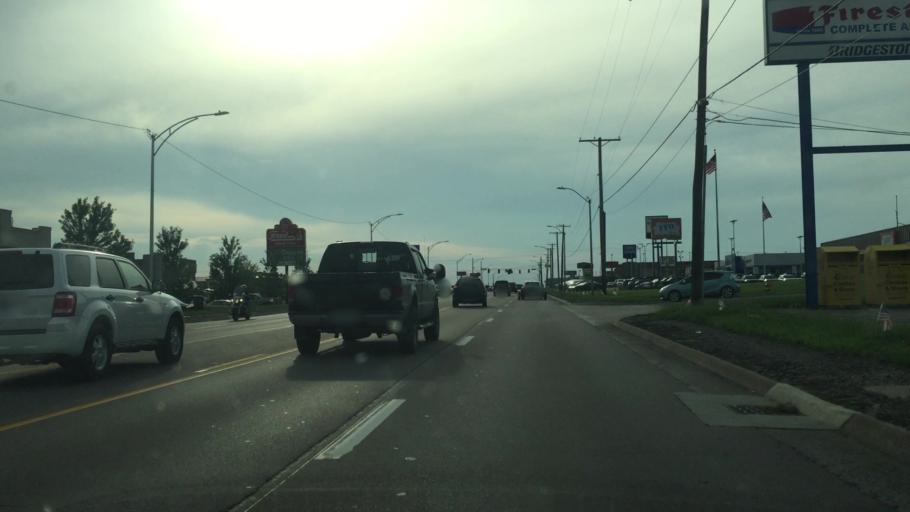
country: US
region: Missouri
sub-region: Pettis County
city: Sedalia
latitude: 38.7092
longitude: -93.2669
